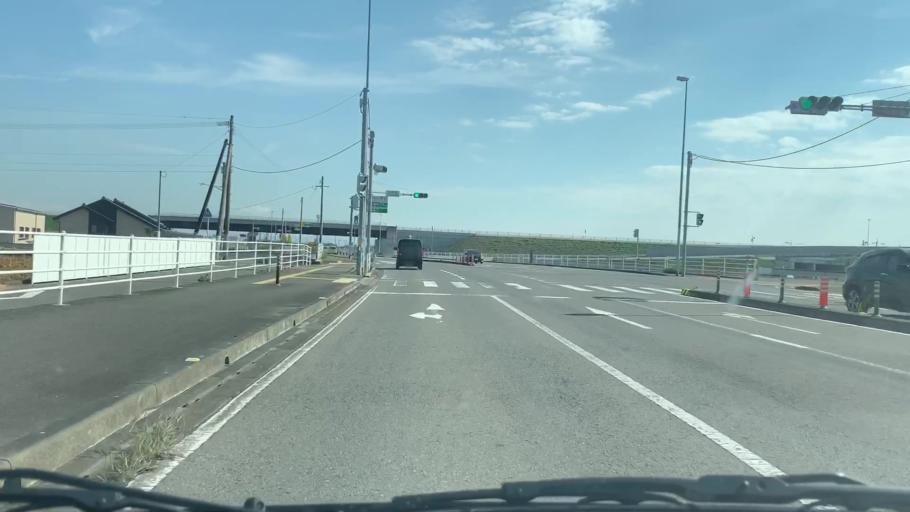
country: JP
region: Saga Prefecture
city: Saga-shi
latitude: 33.2207
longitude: 130.2124
